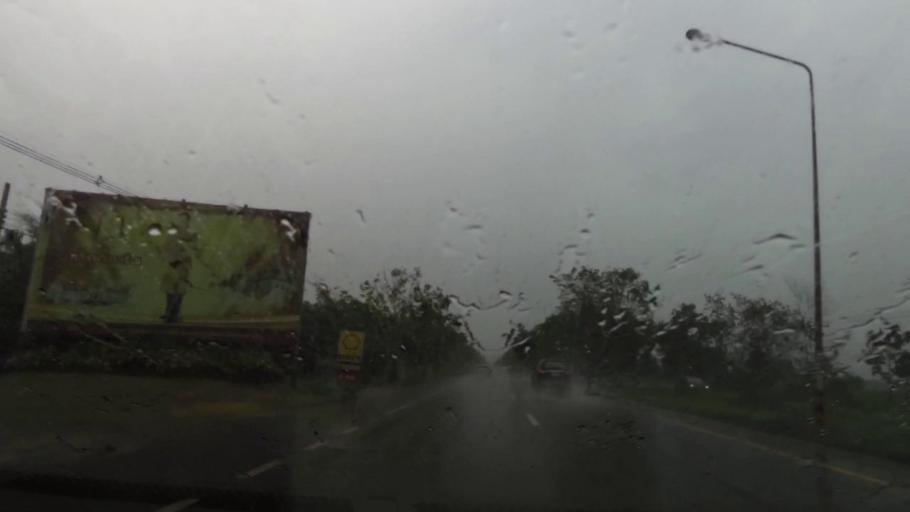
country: TH
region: Rayong
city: Wang Chan
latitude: 12.9960
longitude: 101.4850
